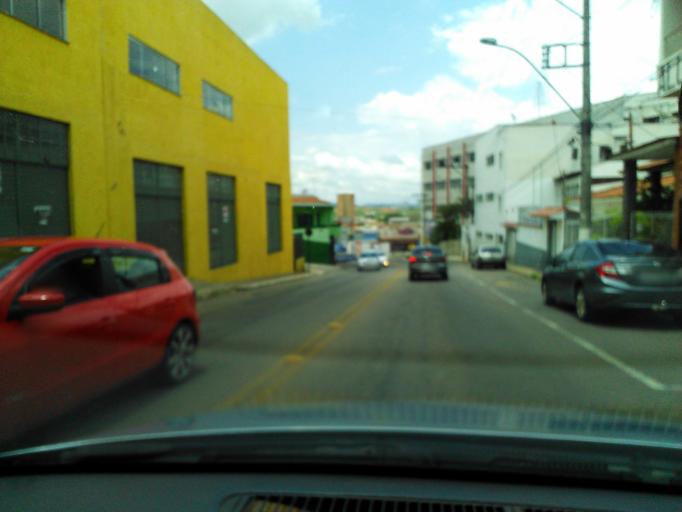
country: BR
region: Minas Gerais
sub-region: Tres Coracoes
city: Tres Coracoes
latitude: -21.6921
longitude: -45.2591
